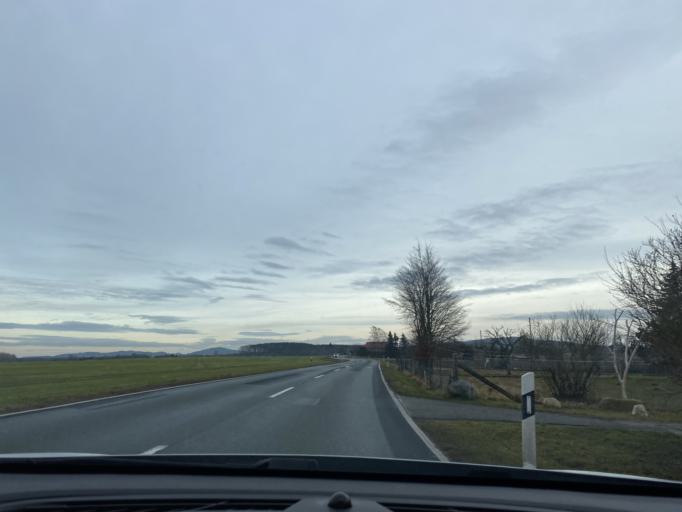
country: DE
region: Saxony
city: Reichenbach
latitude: 51.1219
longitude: 14.8246
